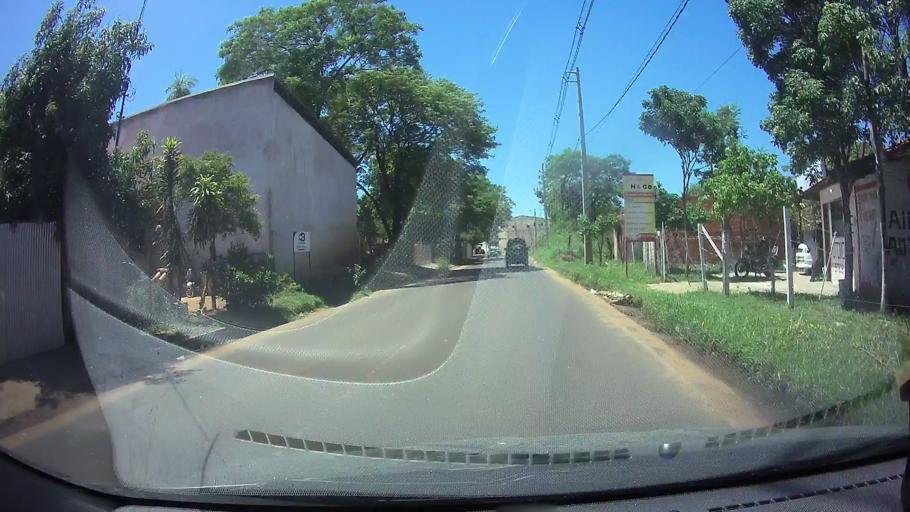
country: PY
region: Central
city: San Lorenzo
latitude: -25.2843
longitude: -57.4947
